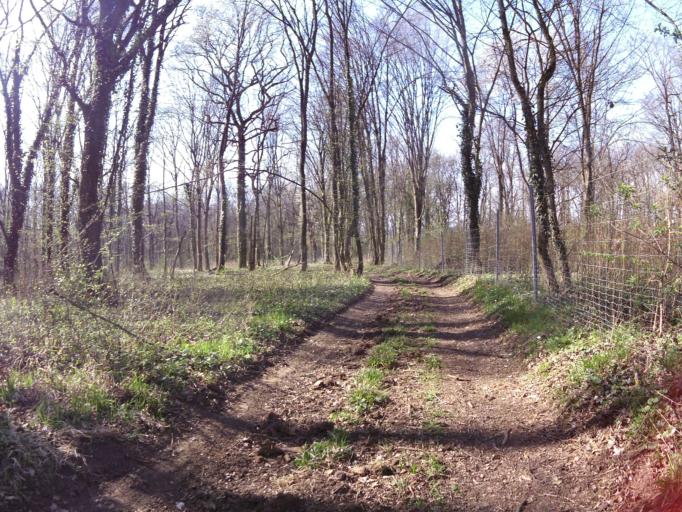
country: DE
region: Bavaria
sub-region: Regierungsbezirk Unterfranken
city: Kurnach
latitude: 49.8314
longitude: 10.0553
